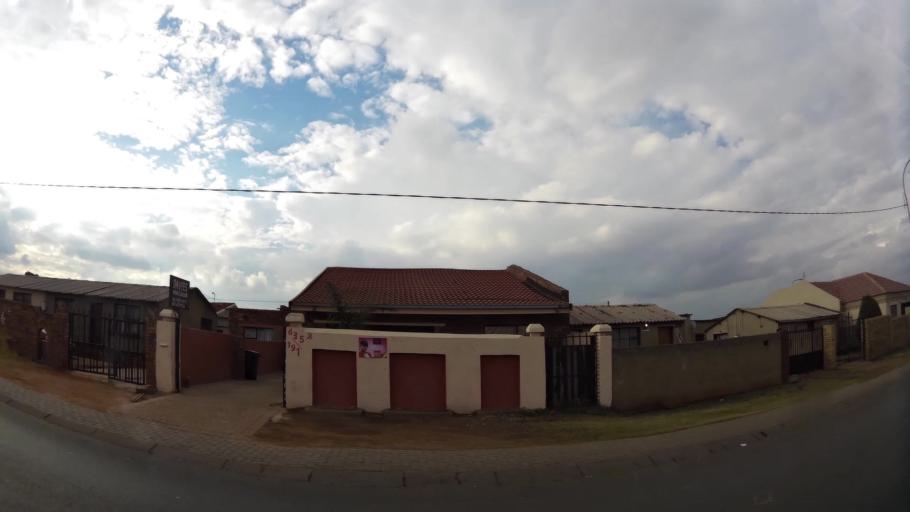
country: ZA
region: Gauteng
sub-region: City of Johannesburg Metropolitan Municipality
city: Soweto
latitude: -26.2542
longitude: 27.8297
